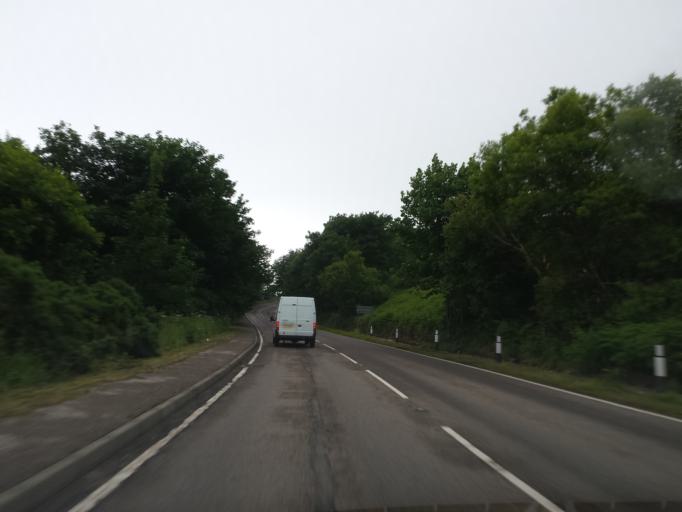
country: GB
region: Scotland
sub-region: Highland
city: Brora
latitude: 58.1126
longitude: -3.6607
